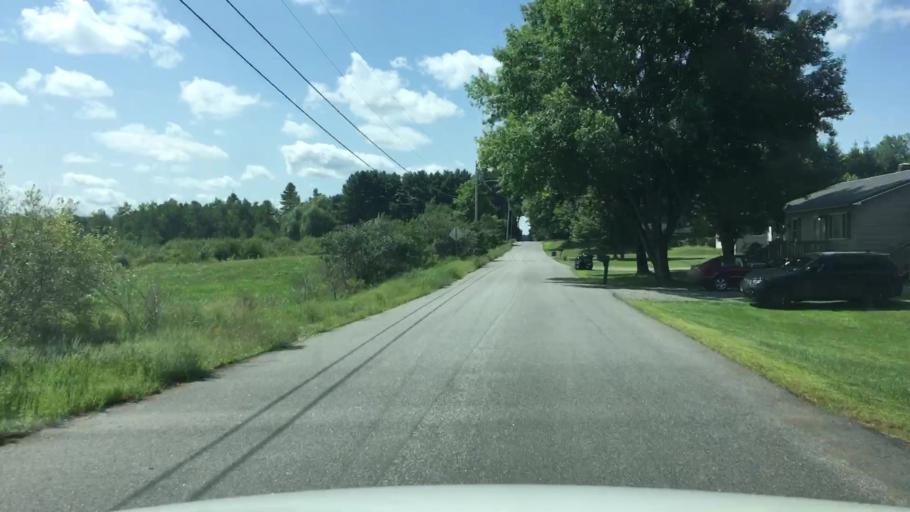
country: US
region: Maine
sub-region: Kennebec County
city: Manchester
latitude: 44.3554
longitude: -69.8262
